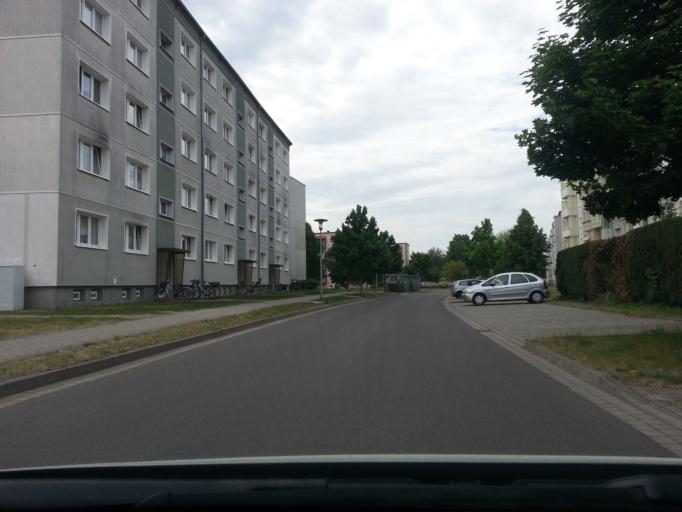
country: DE
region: Mecklenburg-Vorpommern
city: Torgelow
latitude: 53.6372
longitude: 14.0231
